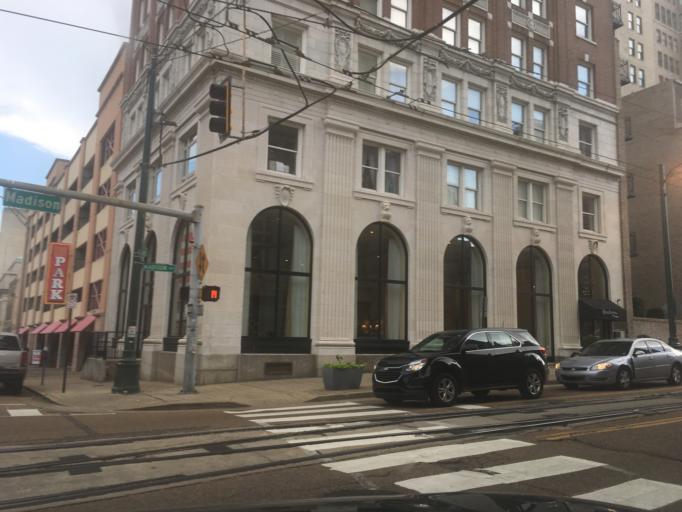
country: US
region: Tennessee
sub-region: Shelby County
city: Memphis
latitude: 35.1450
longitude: -90.0515
